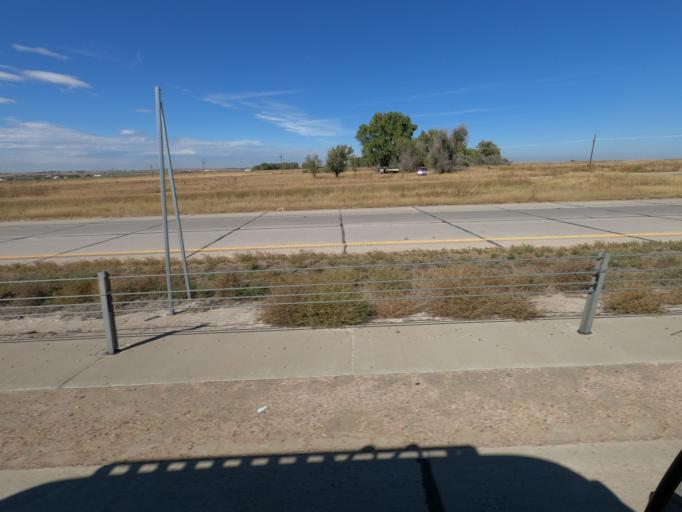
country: US
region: Colorado
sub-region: Weld County
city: Hudson
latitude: 40.0784
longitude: -104.6391
